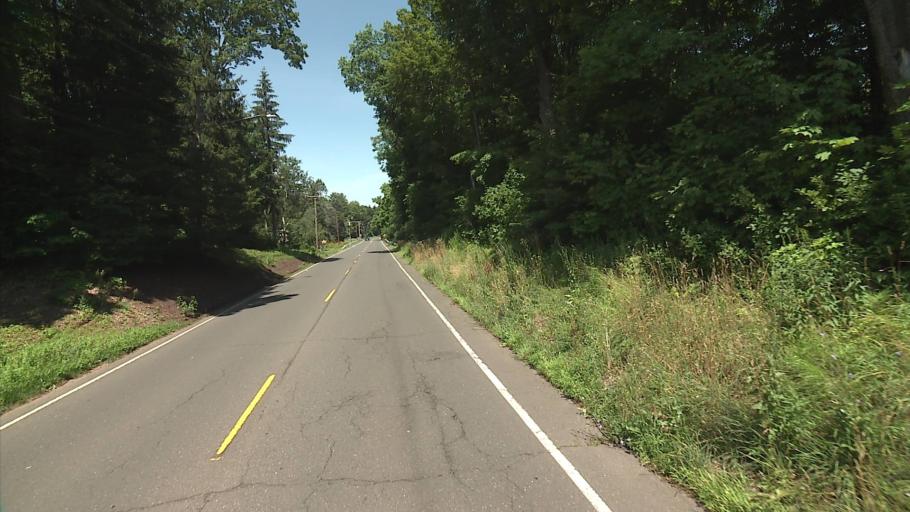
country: US
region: Connecticut
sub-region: Hartford County
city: Kensington
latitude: 41.6425
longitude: -72.7835
